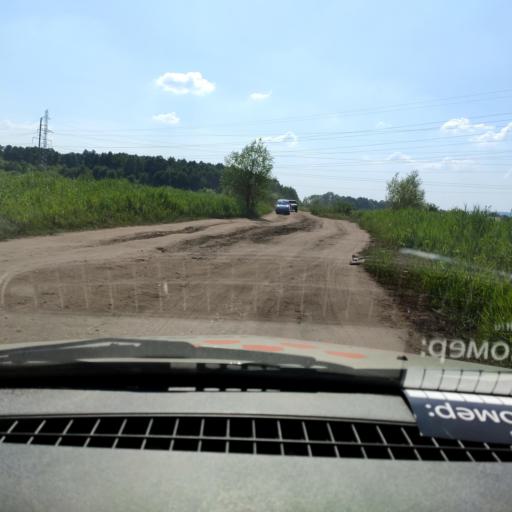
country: RU
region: Bashkortostan
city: Avdon
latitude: 54.6502
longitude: 55.7915
